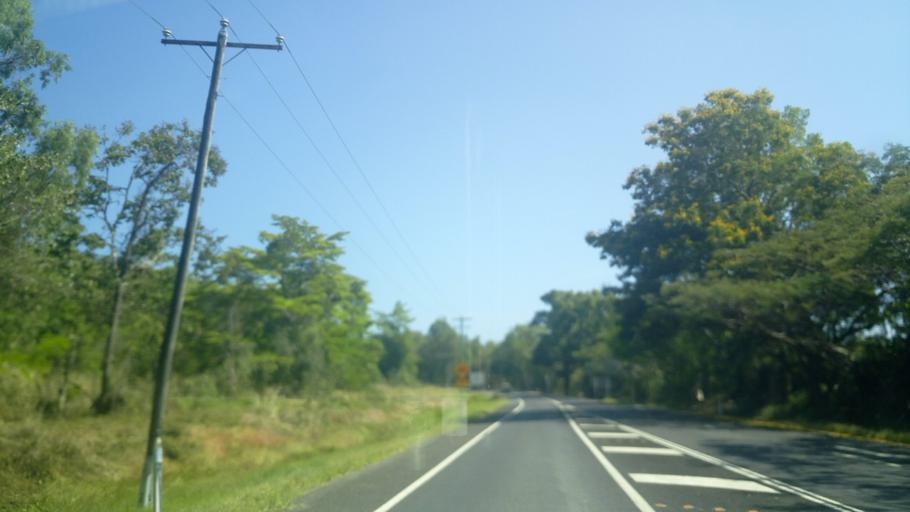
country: AU
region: Queensland
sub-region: Cairns
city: Palm Cove
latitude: -16.7446
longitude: 145.6637
